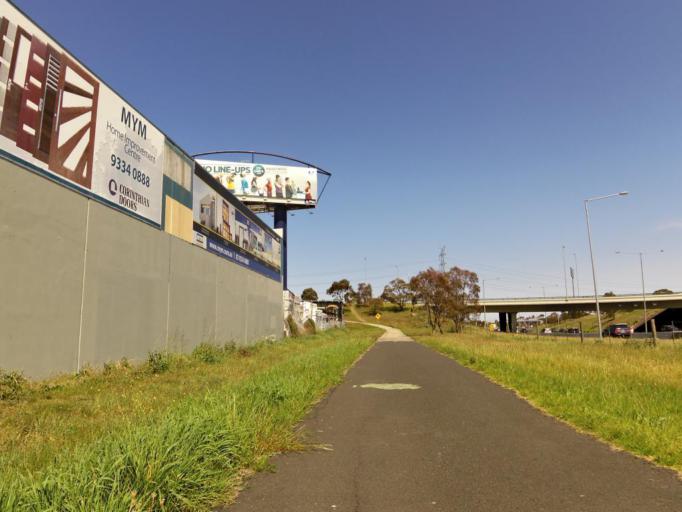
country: AU
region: Victoria
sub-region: Moonee Valley
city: Keilor East
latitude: -37.7375
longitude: 144.8522
